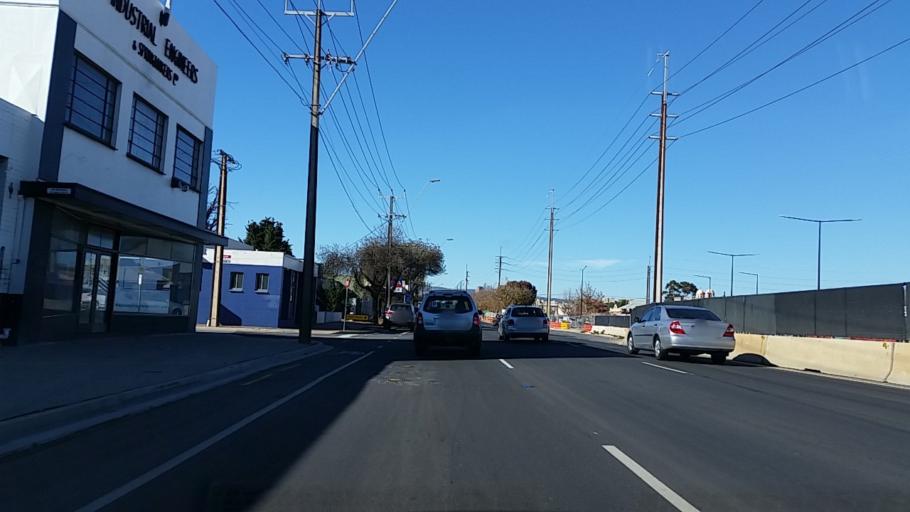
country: AU
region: South Australia
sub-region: Charles Sturt
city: Allenby Gardens
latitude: -34.9020
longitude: 138.5675
